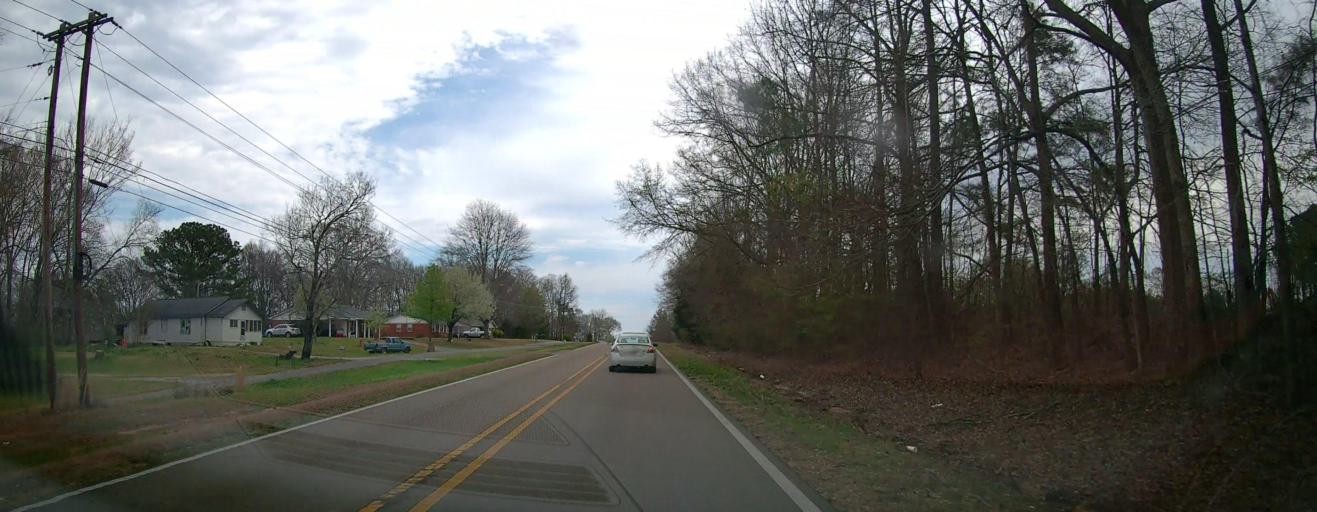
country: US
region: Mississippi
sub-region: Itawamba County
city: Fulton
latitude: 34.2711
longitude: -88.3391
